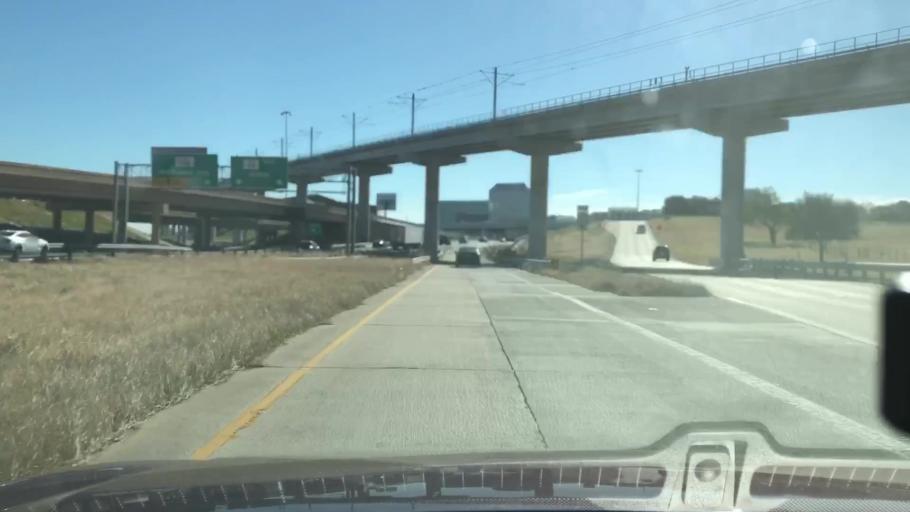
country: US
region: Texas
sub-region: Dallas County
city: Irving
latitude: 32.8822
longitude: -96.9498
